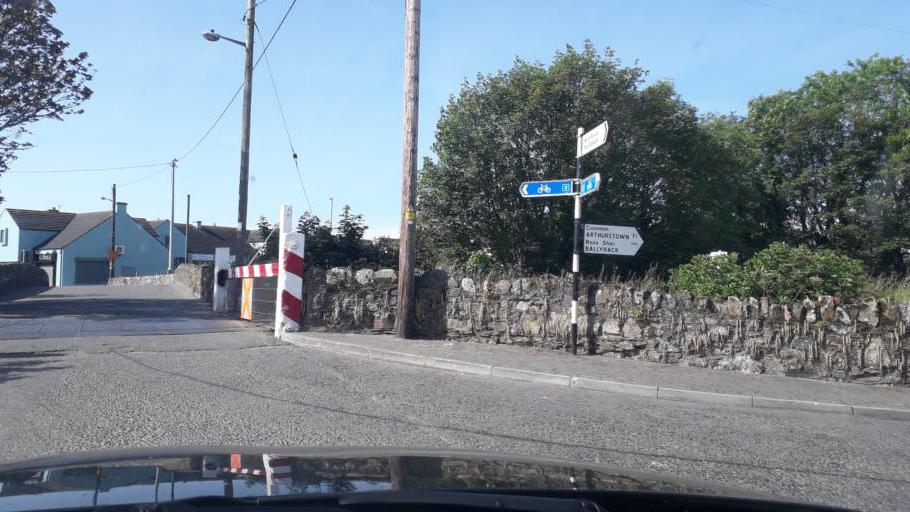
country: IE
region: Leinster
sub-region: Loch Garman
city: Loch Garman
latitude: 52.2311
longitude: -6.5528
